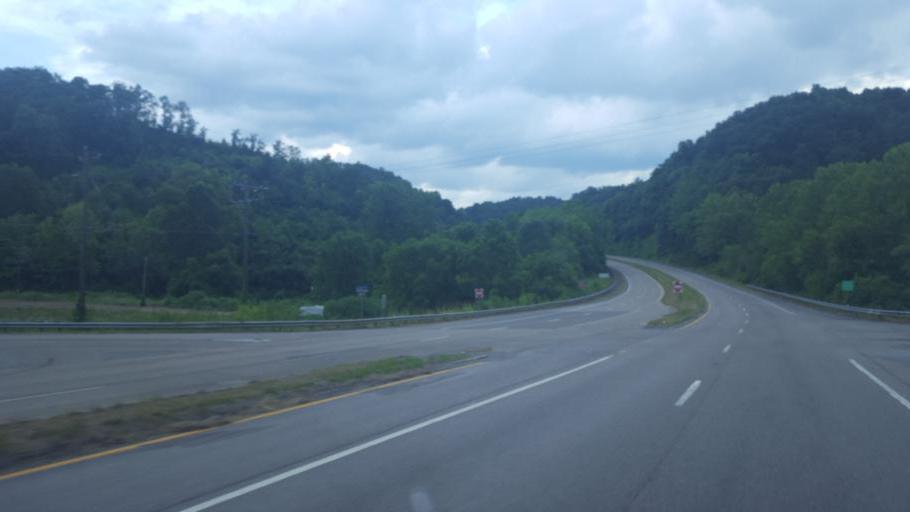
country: US
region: Virginia
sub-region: Wise County
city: Pound
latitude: 37.1172
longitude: -82.6185
